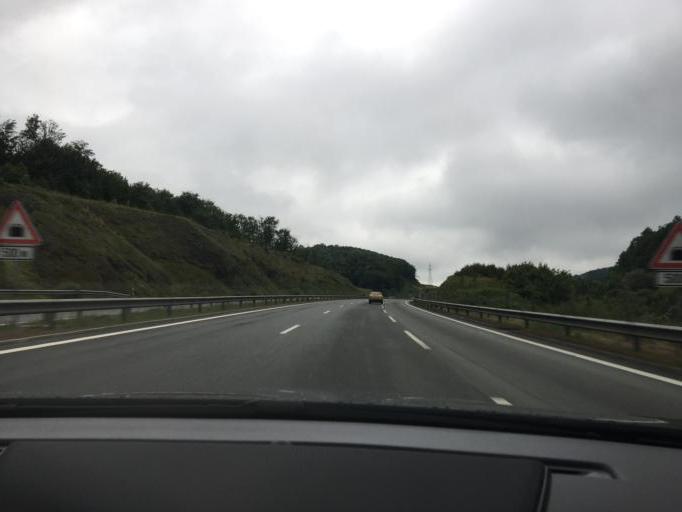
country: BG
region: Sofiya
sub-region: Obshtina Bozhurishte
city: Bozhurishte
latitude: 42.6631
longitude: 23.1452
